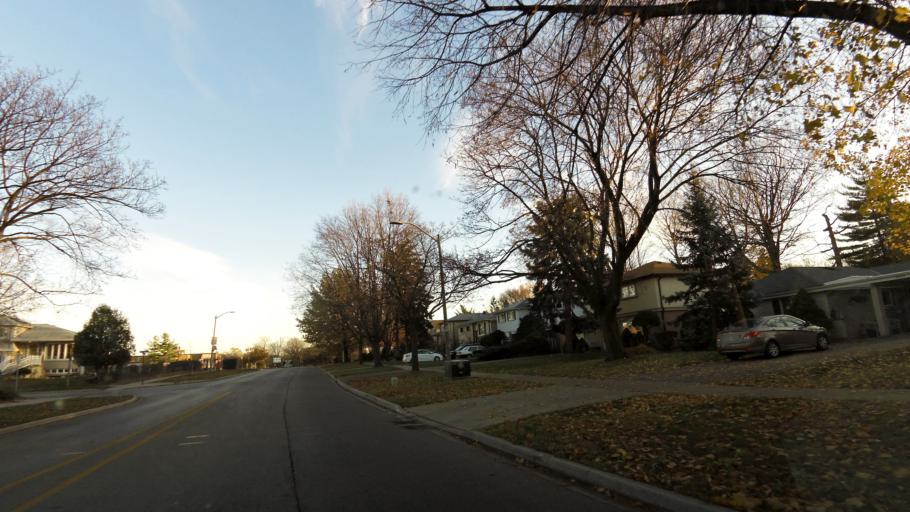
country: CA
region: Ontario
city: Etobicoke
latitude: 43.6277
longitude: -79.5949
